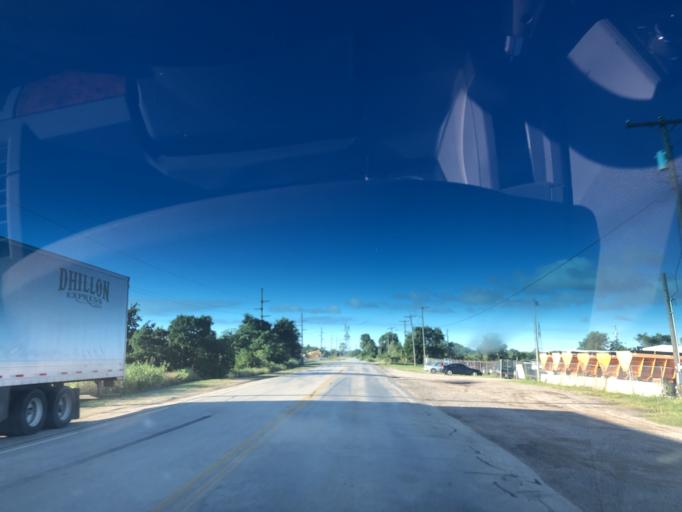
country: US
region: Texas
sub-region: Dallas County
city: Grand Prairie
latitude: 32.7908
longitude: -97.0172
